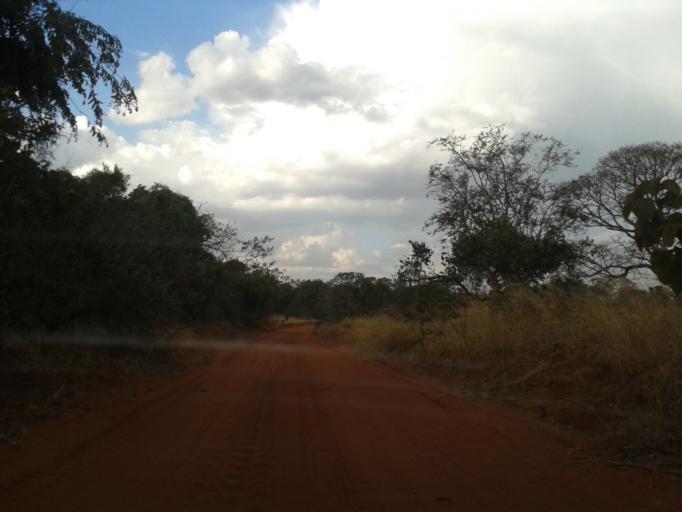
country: BR
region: Minas Gerais
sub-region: Santa Vitoria
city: Santa Vitoria
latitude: -19.1924
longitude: -49.8767
